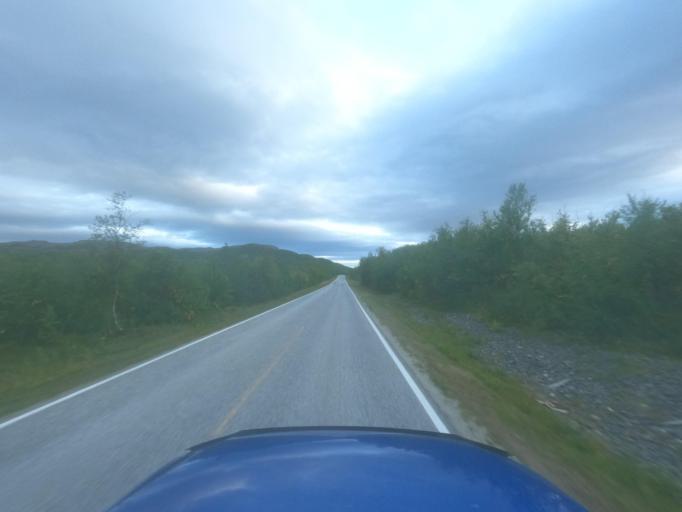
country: NO
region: Finnmark Fylke
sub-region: Porsanger
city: Lakselv
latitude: 69.9705
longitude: 24.9702
